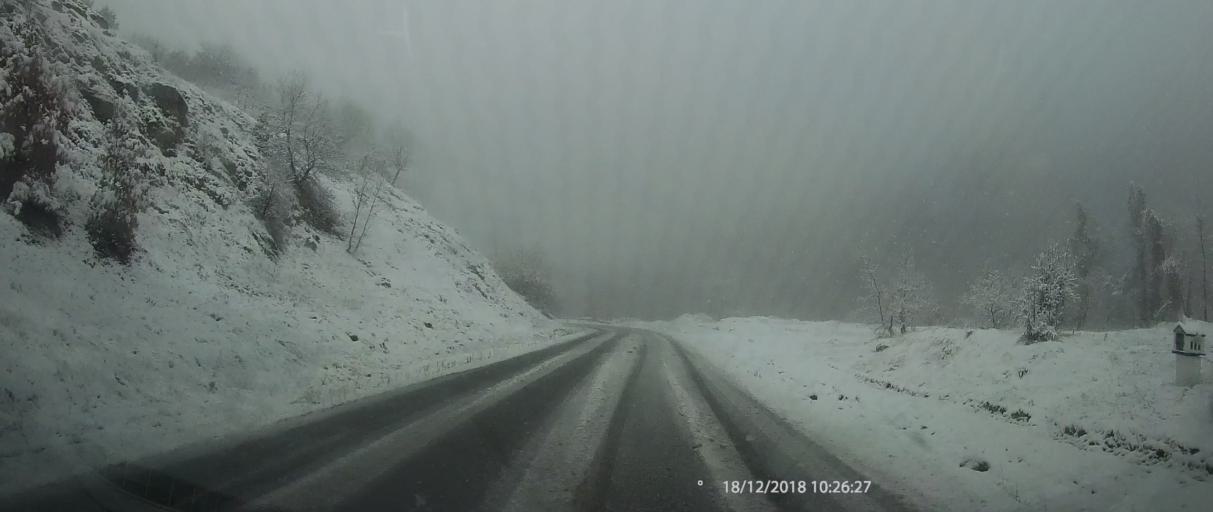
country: GR
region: Thessaly
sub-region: Nomos Larisis
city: Livadi
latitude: 40.1694
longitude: 22.2521
